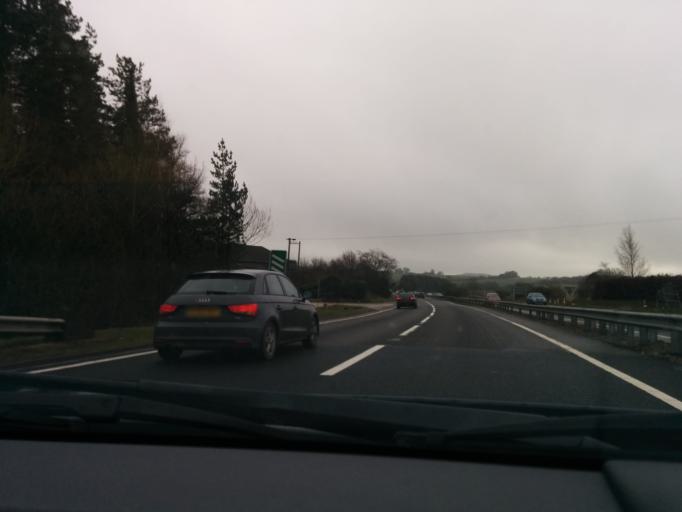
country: GB
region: England
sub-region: West Berkshire
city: Hermitage
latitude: 51.5044
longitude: -1.2940
